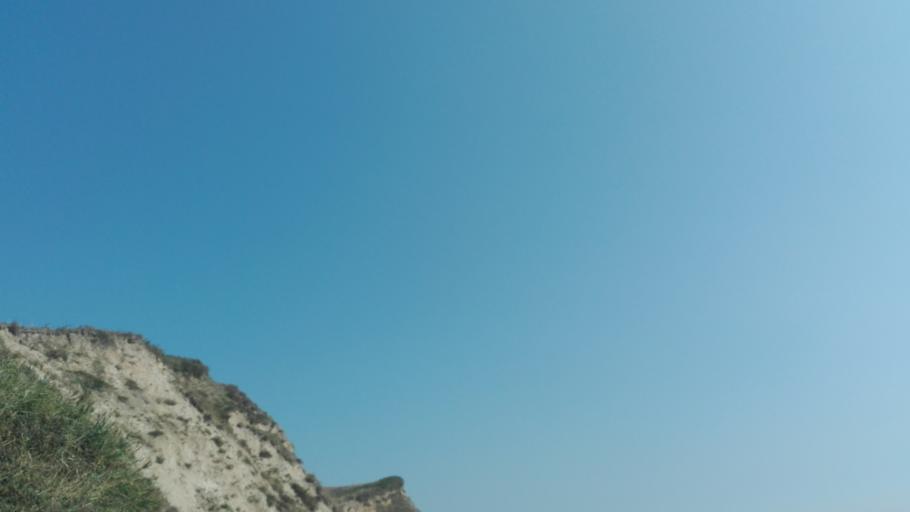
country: DK
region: Central Jutland
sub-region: Arhus Kommune
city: Logten
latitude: 56.1623
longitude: 10.4048
